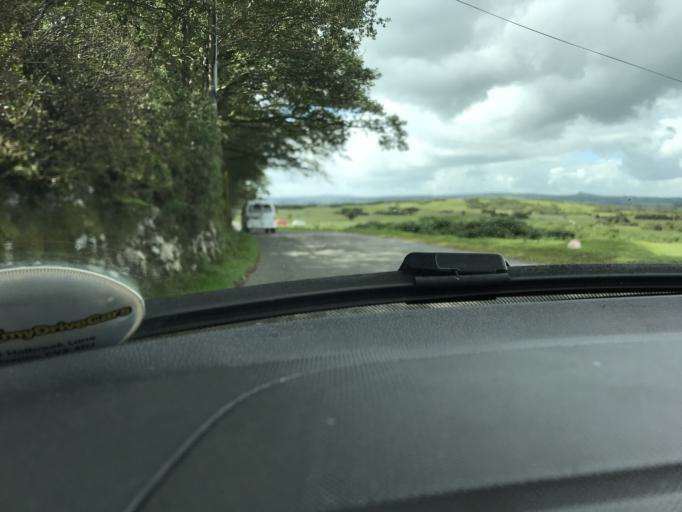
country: GB
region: England
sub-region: Devon
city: Horrabridge
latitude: 50.5411
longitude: -4.0989
